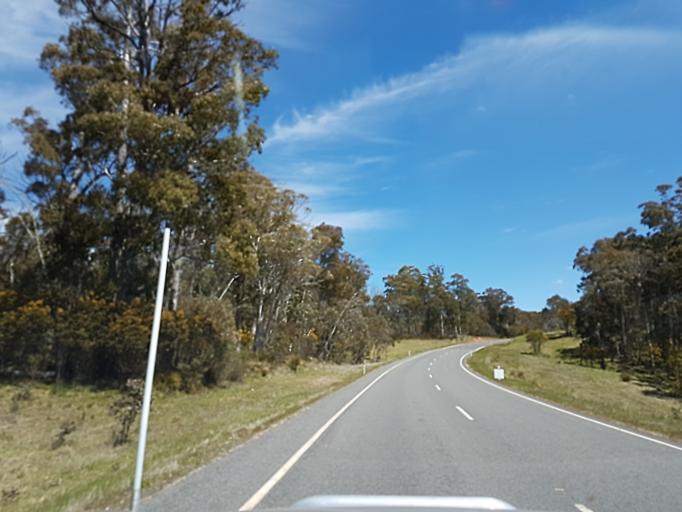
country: AU
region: Victoria
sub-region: Alpine
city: Mount Beauty
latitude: -37.0822
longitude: 147.3625
